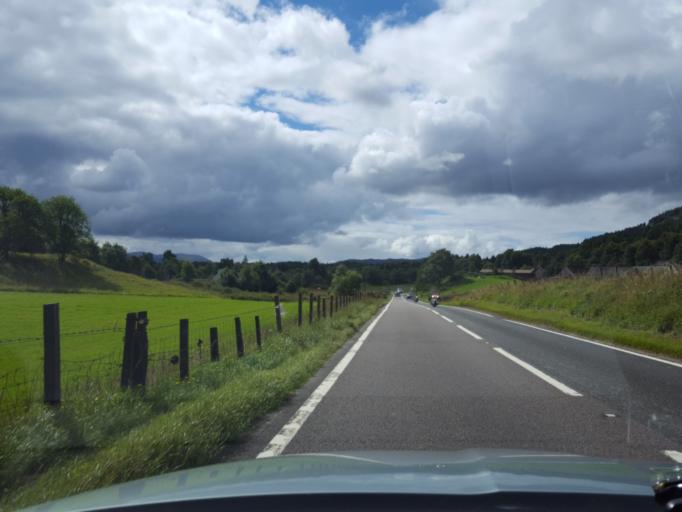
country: GB
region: Scotland
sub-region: Highland
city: Aviemore
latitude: 57.2295
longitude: -3.8137
